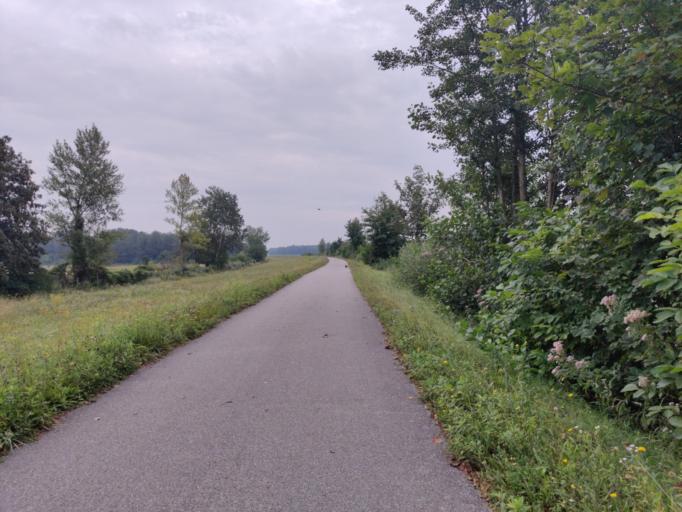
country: AT
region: Upper Austria
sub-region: Politischer Bezirk Urfahr-Umgebung
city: Steyregg
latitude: 48.2610
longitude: 14.3978
